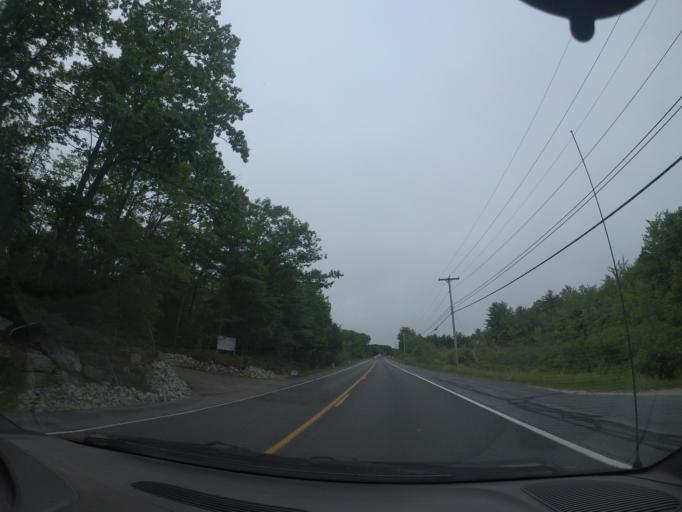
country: US
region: Maine
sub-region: York County
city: Arundel
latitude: 43.4367
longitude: -70.5040
